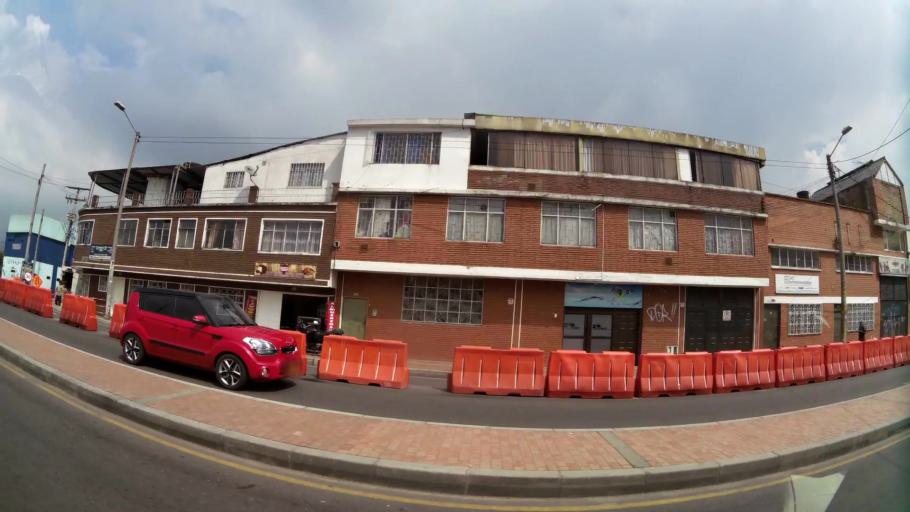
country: CO
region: Bogota D.C.
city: Bogota
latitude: 4.6237
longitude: -74.0922
